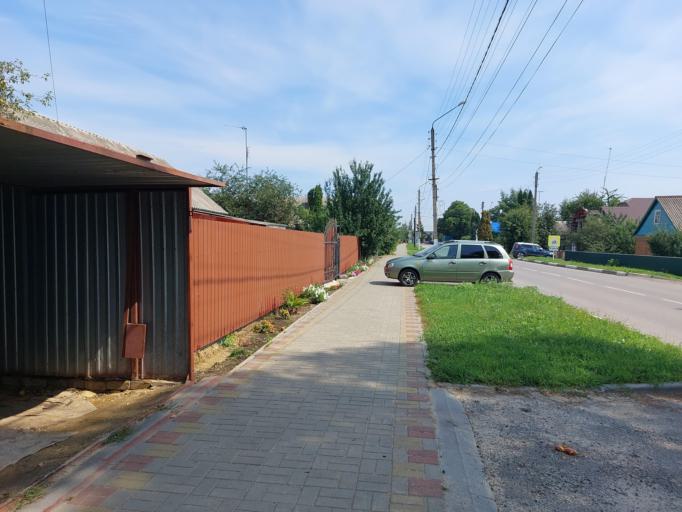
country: RU
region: Lipetsk
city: Dolgorukovo
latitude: 52.3240
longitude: 38.3588
